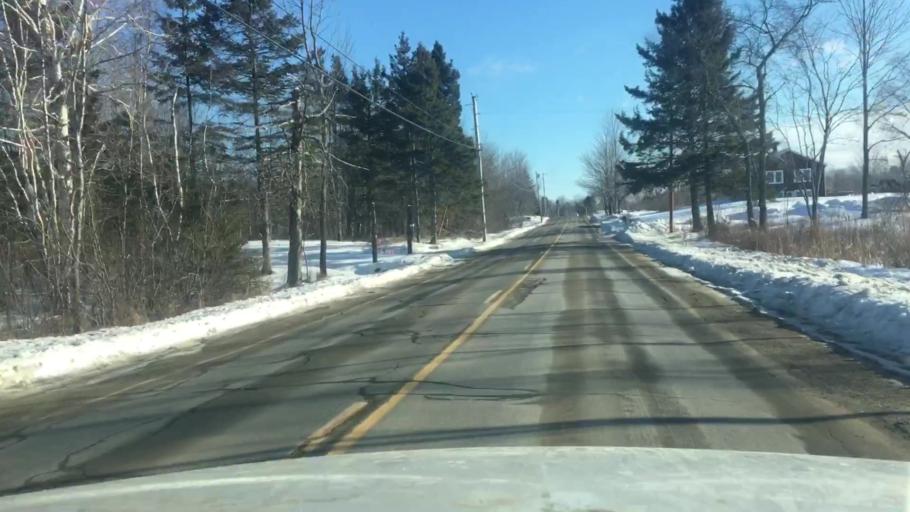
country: US
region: Maine
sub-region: Hancock County
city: Ellsworth
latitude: 44.5938
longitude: -68.4100
